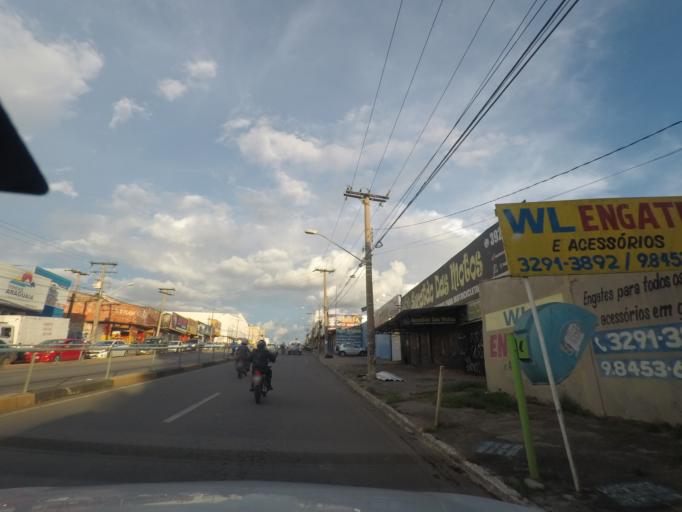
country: BR
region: Goias
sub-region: Goiania
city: Goiania
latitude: -16.6705
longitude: -49.2973
